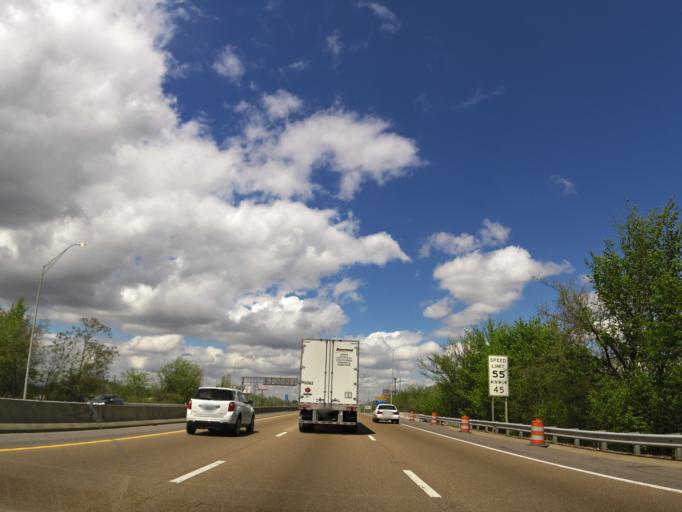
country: US
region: Tennessee
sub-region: Shelby County
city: Memphis
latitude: 35.1799
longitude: -90.0179
